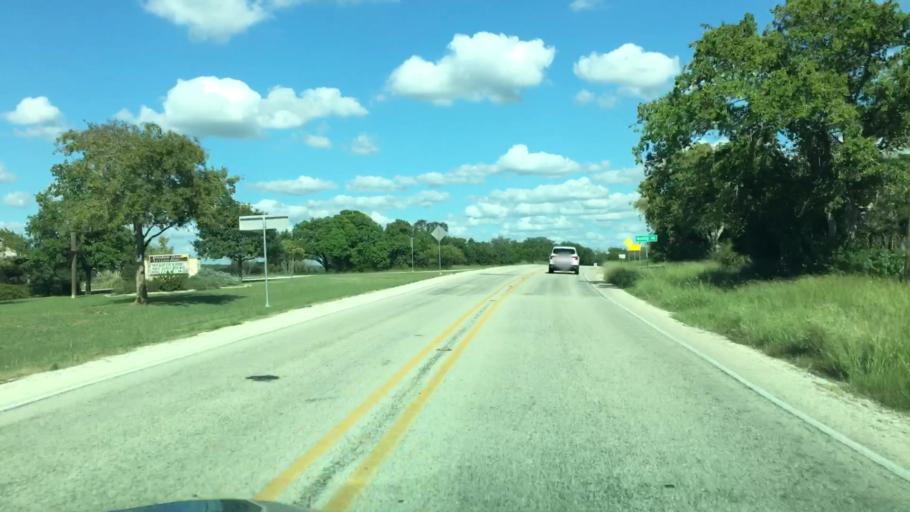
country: US
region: Texas
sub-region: Blanco County
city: Blanco
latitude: 30.0922
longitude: -98.4143
